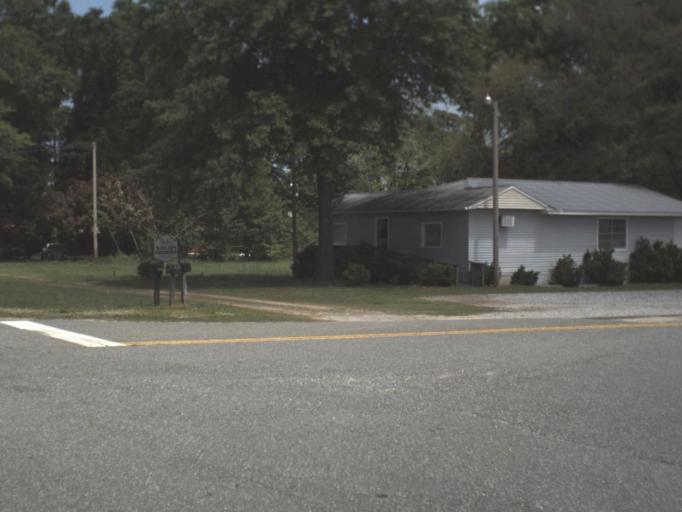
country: US
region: Alabama
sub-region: Escambia County
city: East Brewton
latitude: 30.9074
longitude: -87.0334
